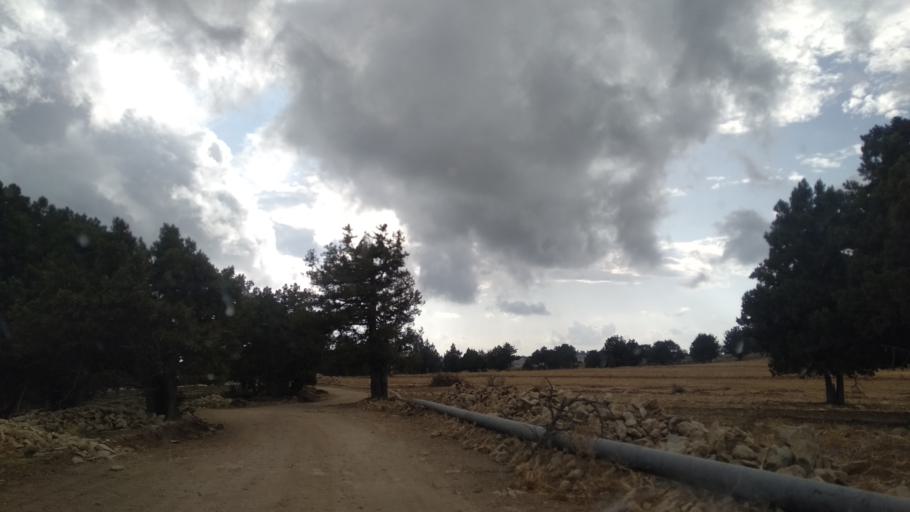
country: TR
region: Mersin
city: Sarikavak
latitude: 36.5688
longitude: 33.7435
